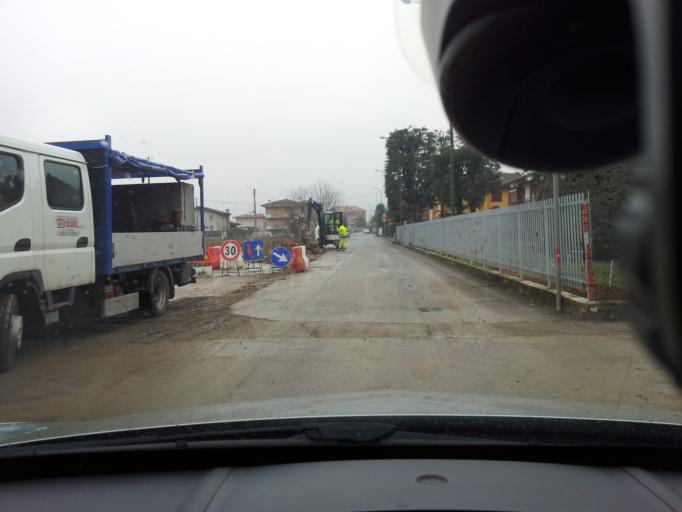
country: IT
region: Lombardy
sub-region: Provincia di Bergamo
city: Calcinate
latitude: 45.6132
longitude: 9.7930
